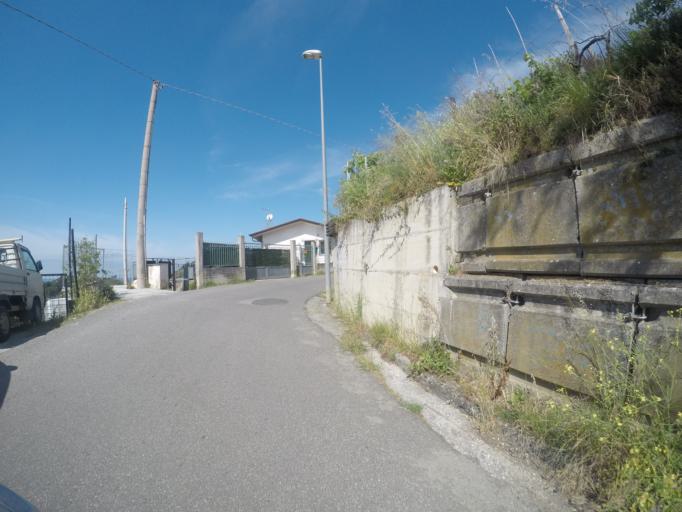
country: IT
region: Tuscany
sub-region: Provincia di Massa-Carrara
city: Massa
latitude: 44.0482
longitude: 10.1209
